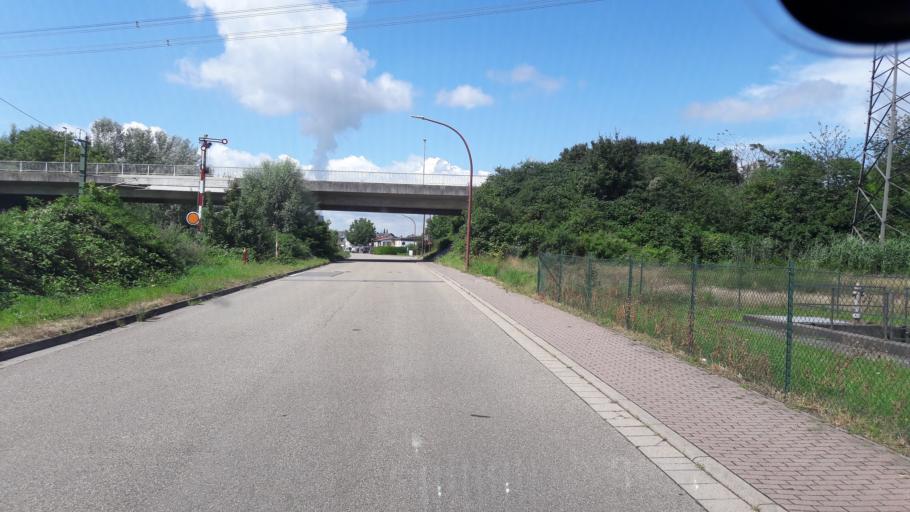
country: DE
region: Baden-Wuerttemberg
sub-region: Karlsruhe Region
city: Philippsburg
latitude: 49.2258
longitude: 8.4616
